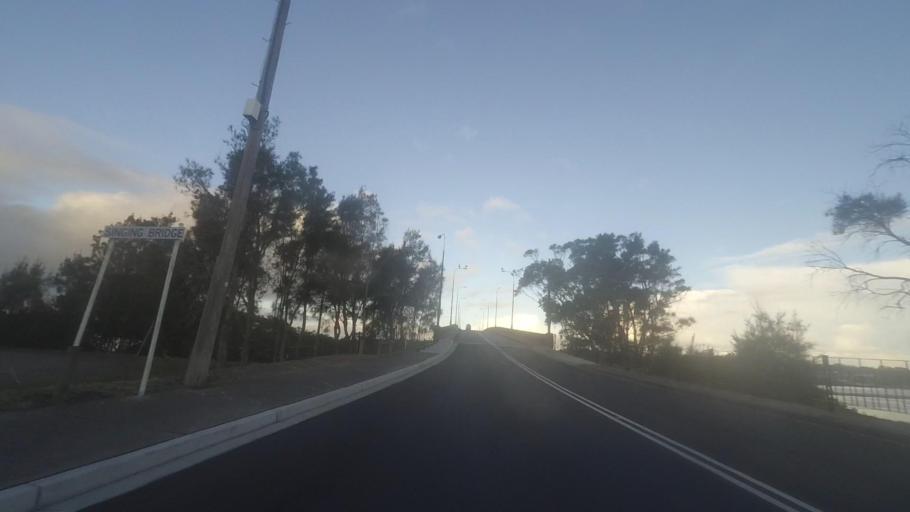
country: AU
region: New South Wales
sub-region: Great Lakes
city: Hawks Nest
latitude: -32.6700
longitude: 152.1665
